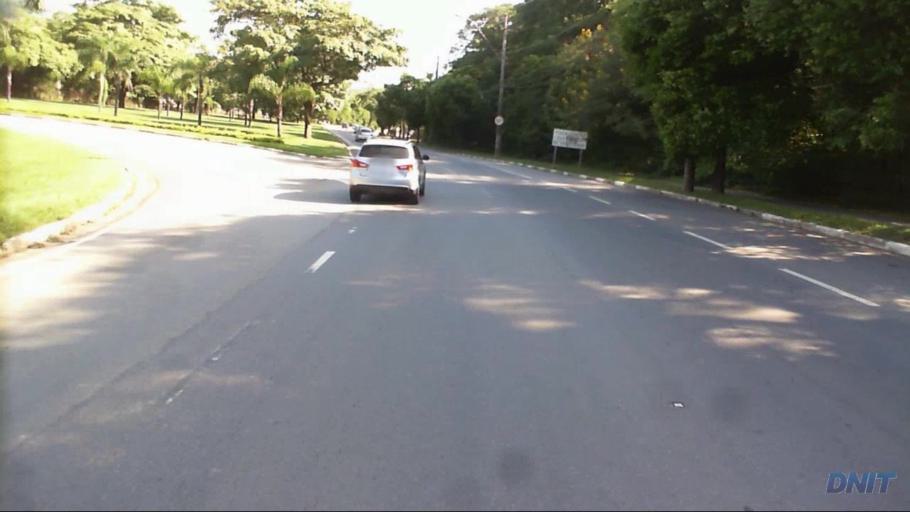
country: BR
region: Minas Gerais
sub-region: Ipatinga
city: Ipatinga
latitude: -19.4868
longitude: -42.5587
